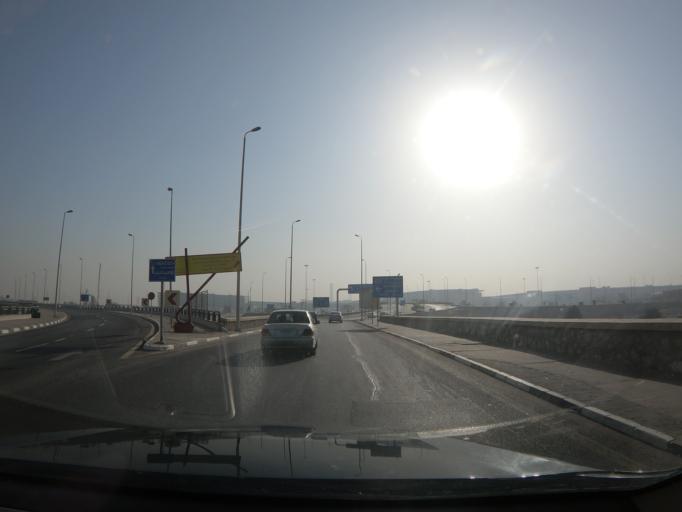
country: EG
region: Muhafazat al Qalyubiyah
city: Al Khankah
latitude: 30.1114
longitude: 31.3904
